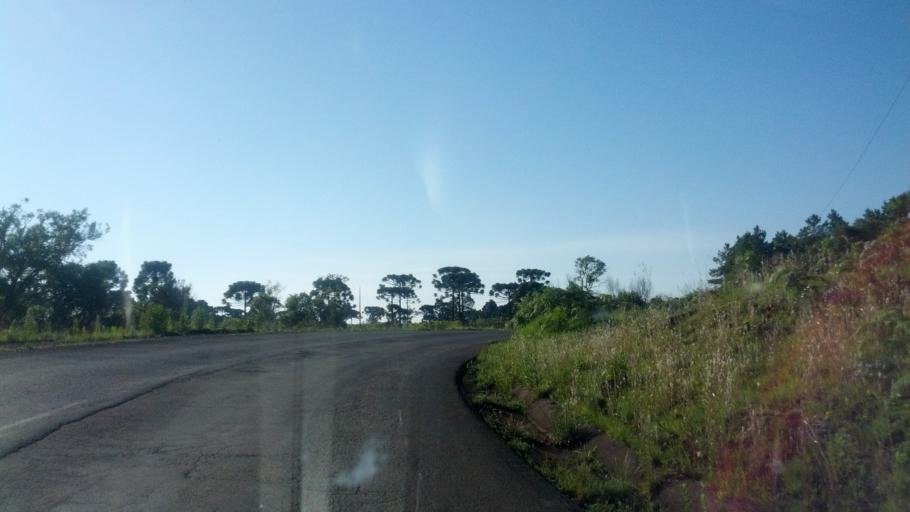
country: BR
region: Santa Catarina
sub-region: Lages
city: Lages
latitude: -27.9507
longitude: -50.4951
